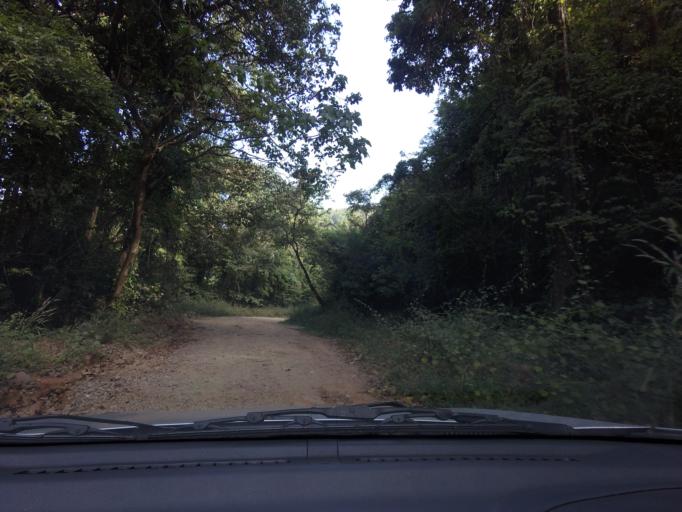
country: IN
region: Karnataka
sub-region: Kodagu
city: Somvarpet
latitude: 12.7171
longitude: 75.6674
